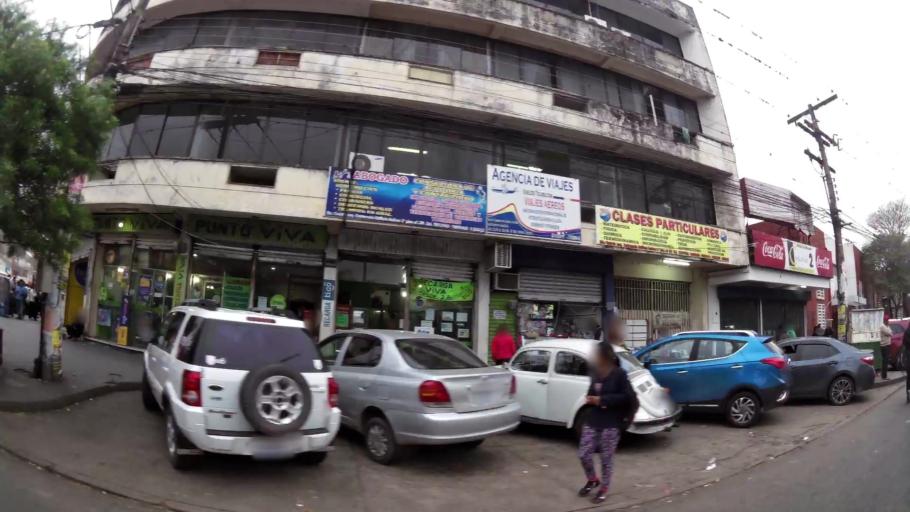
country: BO
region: Santa Cruz
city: Santa Cruz de la Sierra
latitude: -17.7803
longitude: -63.1892
